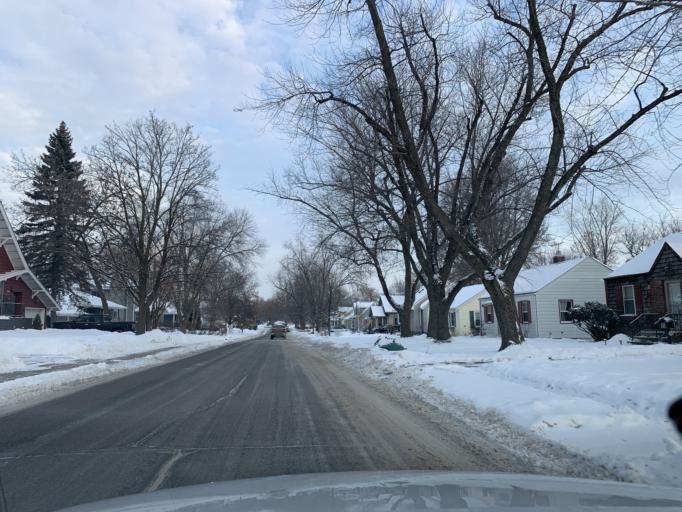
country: US
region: Minnesota
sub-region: Hennepin County
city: Saint Louis Park
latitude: 44.9271
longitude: -93.3531
